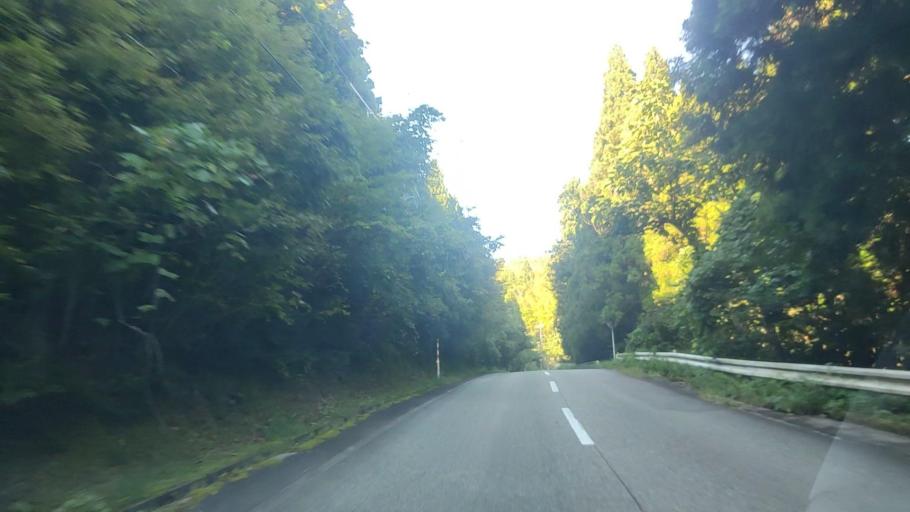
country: JP
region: Ishikawa
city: Nanao
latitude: 37.1135
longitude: 136.9647
